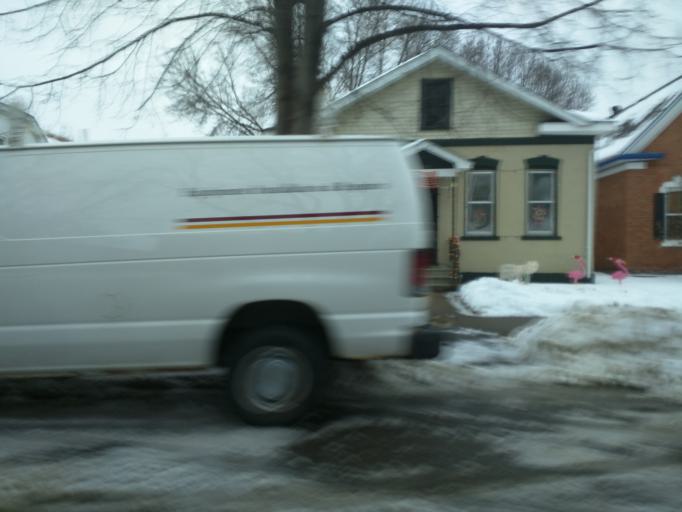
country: US
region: Wisconsin
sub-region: La Crosse County
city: La Crosse
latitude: 43.8010
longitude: -91.2488
